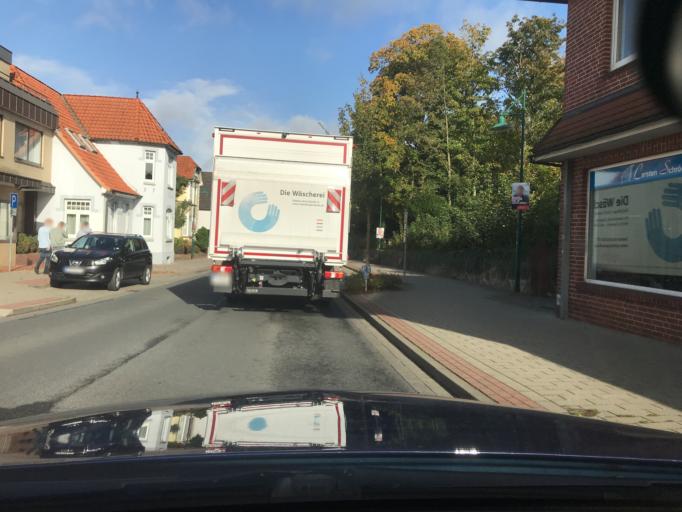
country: DE
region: Lower Saxony
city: Harsefeld
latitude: 53.4525
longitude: 9.5006
